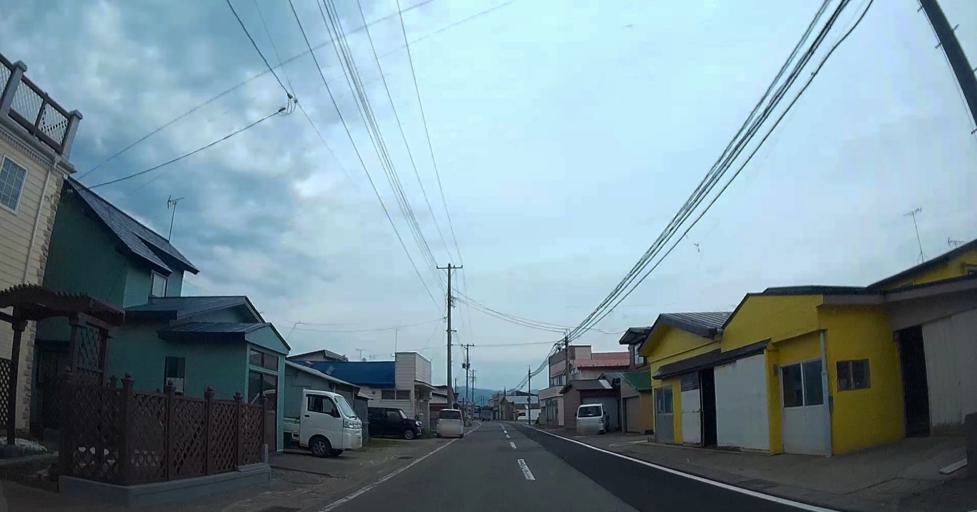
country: JP
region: Aomori
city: Shimokizukuri
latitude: 41.0319
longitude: 140.3276
